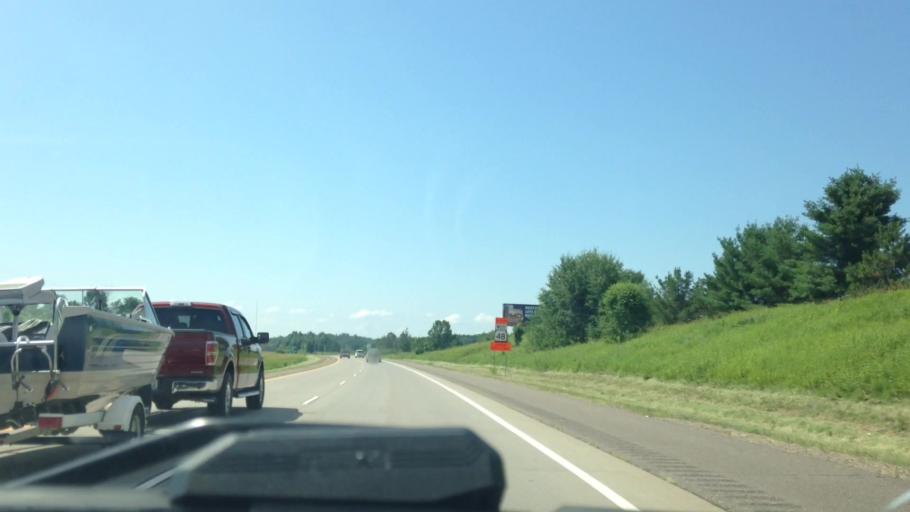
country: US
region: Wisconsin
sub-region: Barron County
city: Rice Lake
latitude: 45.5020
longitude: -91.7639
